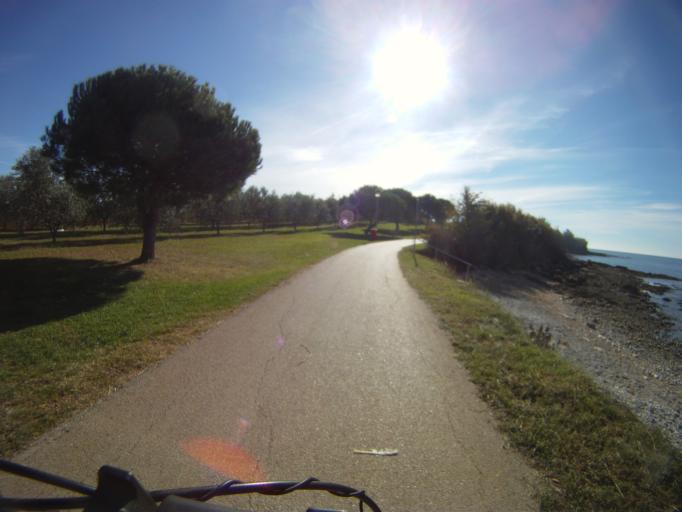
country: HR
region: Istarska
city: Novigrad
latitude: 45.3249
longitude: 13.5526
